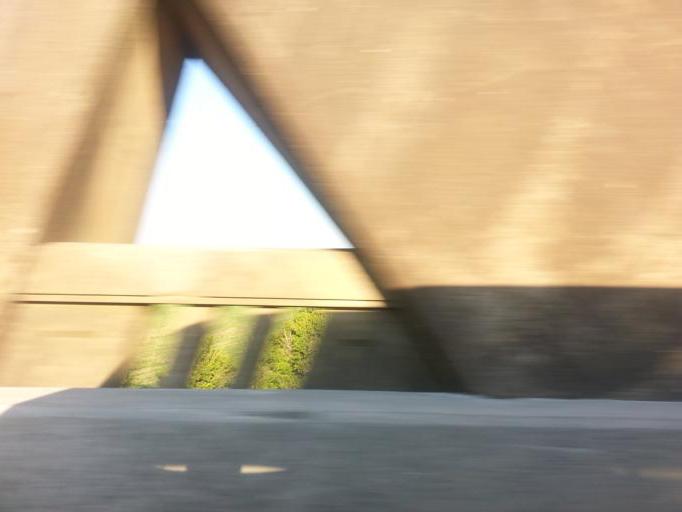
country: US
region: Tennessee
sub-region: Knox County
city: Mascot
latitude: 36.0586
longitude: -83.7042
